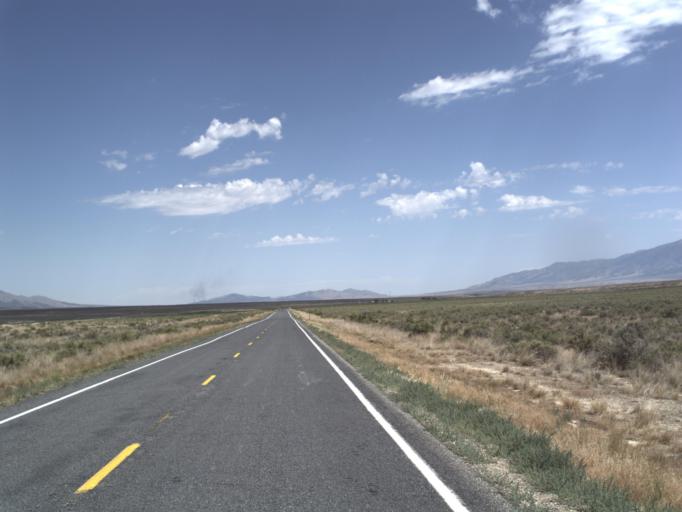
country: US
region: Utah
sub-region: Tooele County
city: Tooele
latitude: 40.1355
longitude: -112.4308
